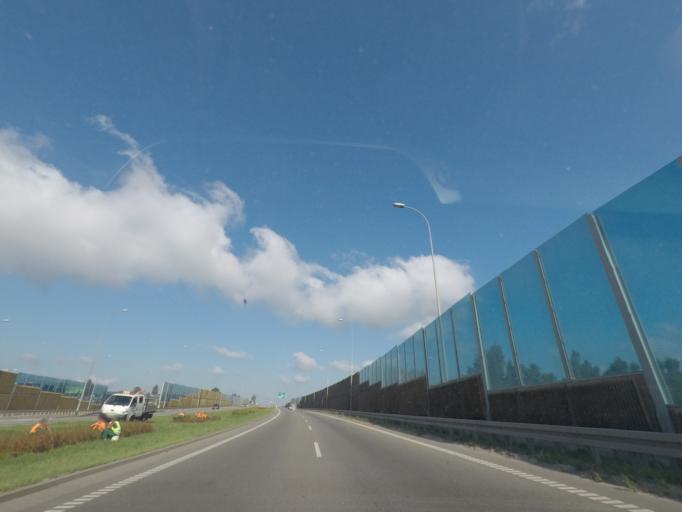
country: PL
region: Pomeranian Voivodeship
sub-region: Powiat gdanski
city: Kowale
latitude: 54.3457
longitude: 18.5419
